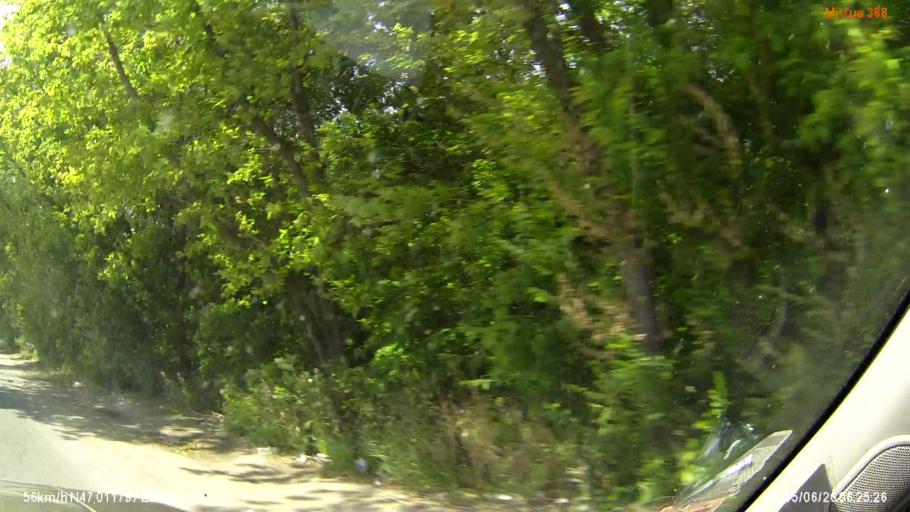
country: MD
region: Chisinau
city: Chisinau
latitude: 47.0119
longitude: 28.8727
